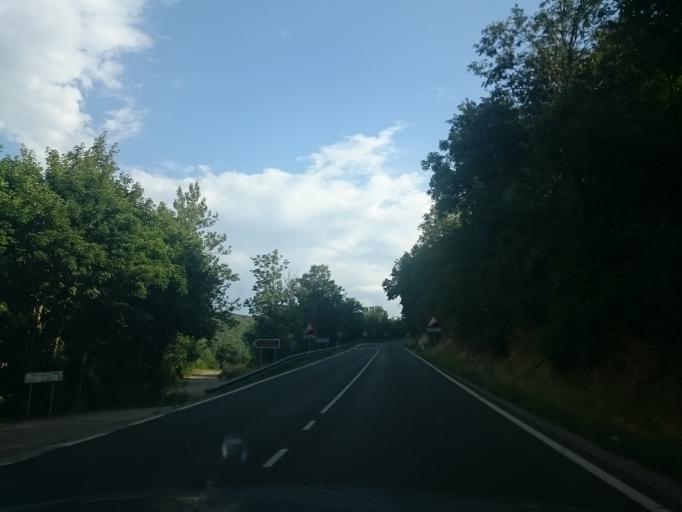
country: ES
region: Castille and Leon
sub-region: Provincia de Burgos
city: Espinosa del Camino
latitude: 42.3842
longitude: -3.3091
